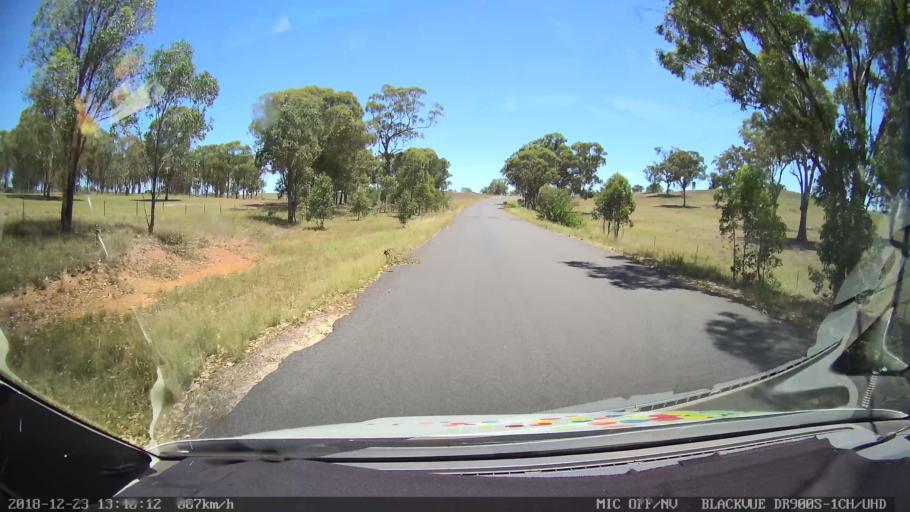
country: AU
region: New South Wales
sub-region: Armidale Dumaresq
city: Armidale
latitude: -30.4648
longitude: 151.1935
